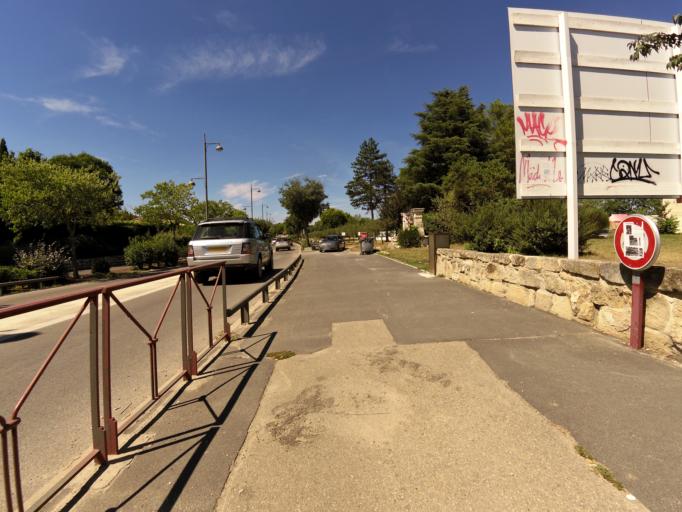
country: FR
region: Languedoc-Roussillon
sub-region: Departement du Gard
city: Sommieres
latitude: 43.7866
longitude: 4.0839
